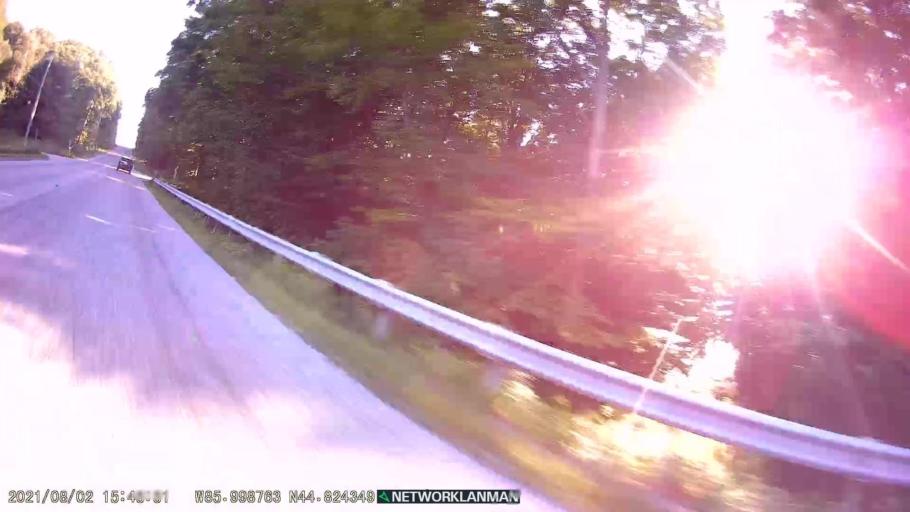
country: US
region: Michigan
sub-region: Benzie County
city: Beulah
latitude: 44.8243
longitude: -85.9988
